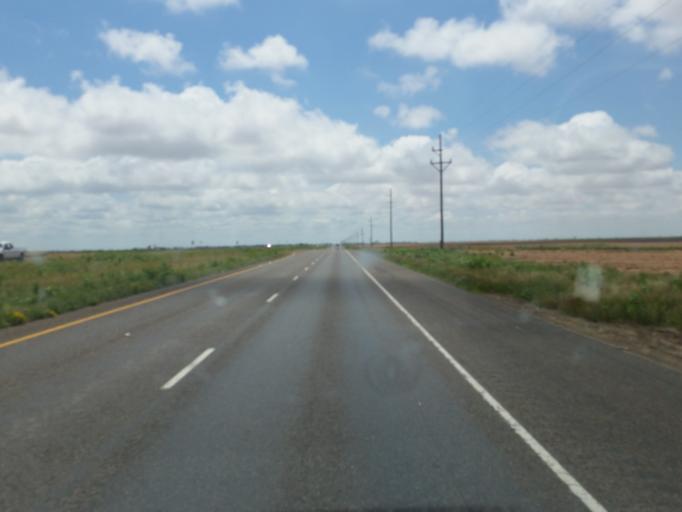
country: US
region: Texas
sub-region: Lubbock County
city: Slaton
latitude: 33.3900
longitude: -101.5988
